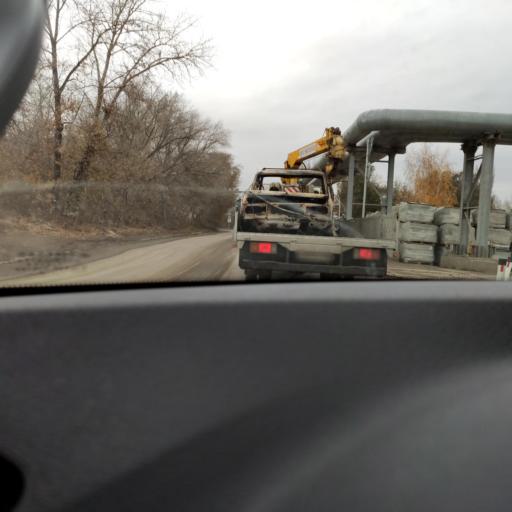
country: RU
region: Samara
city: Smyshlyayevka
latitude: 53.2054
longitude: 50.3014
